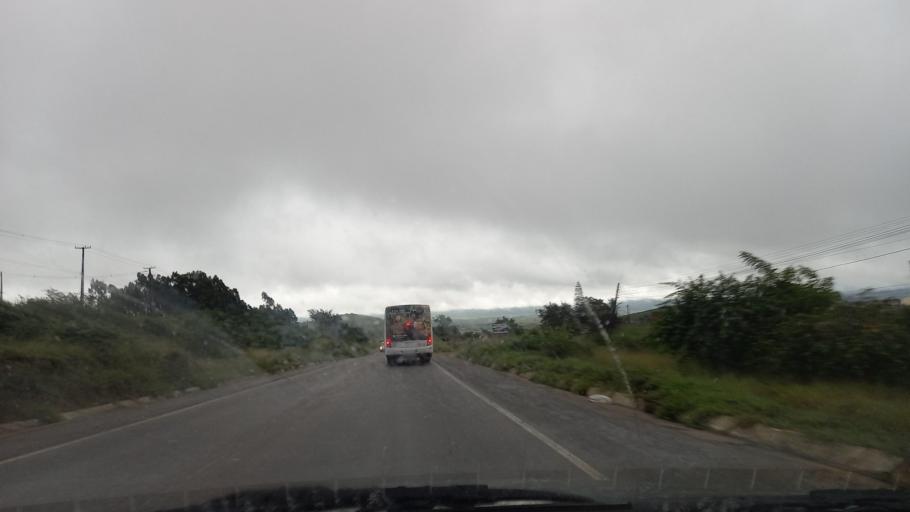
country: BR
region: Pernambuco
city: Garanhuns
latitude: -8.8726
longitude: -36.5073
